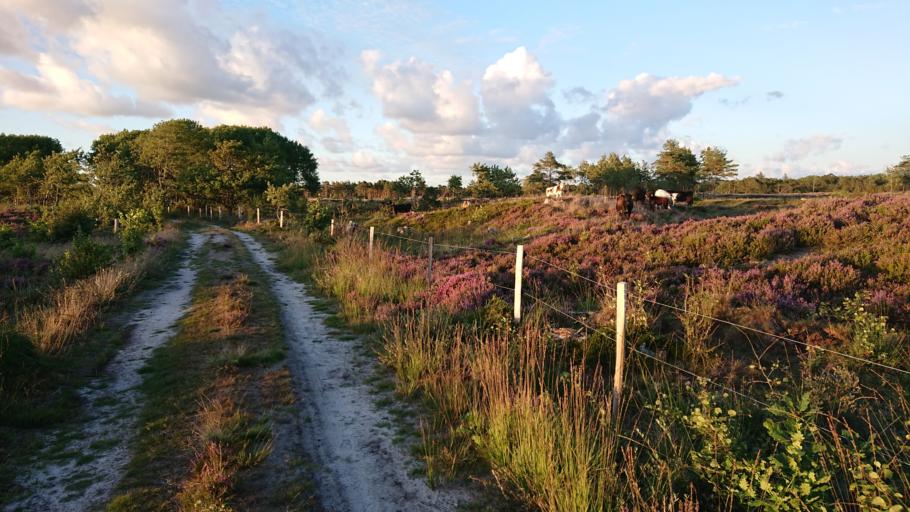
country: DK
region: North Denmark
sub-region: Frederikshavn Kommune
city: Strandby
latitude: 57.5610
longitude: 10.3522
